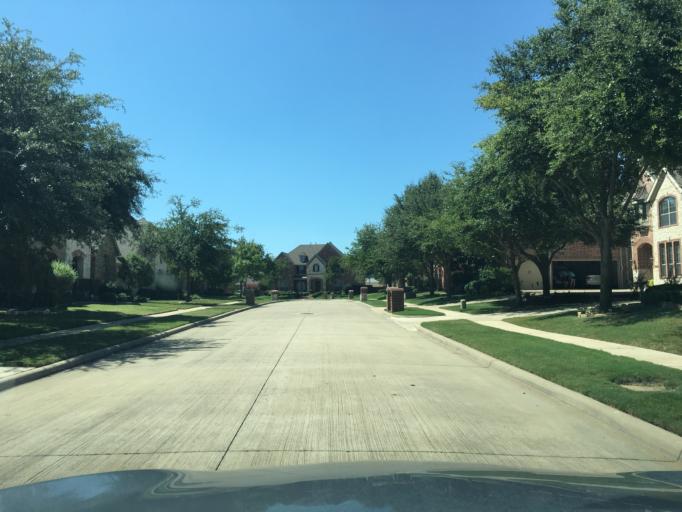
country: US
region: Texas
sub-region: Dallas County
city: Sachse
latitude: 32.9698
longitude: -96.6135
